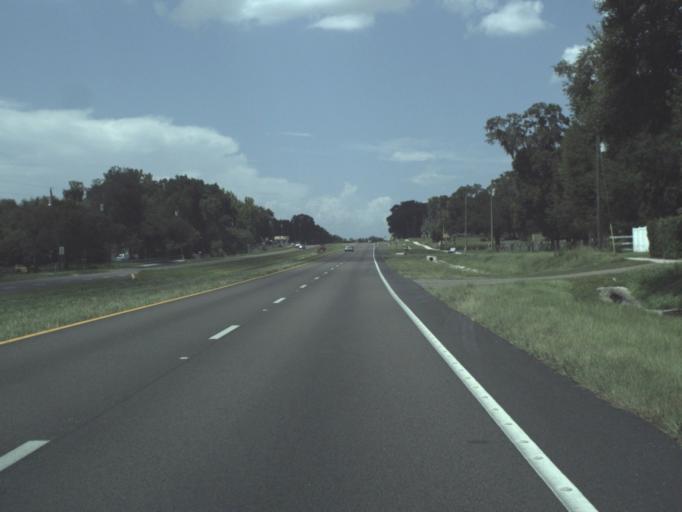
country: US
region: Florida
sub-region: Pasco County
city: Lacoochee
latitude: 28.4302
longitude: -82.1910
